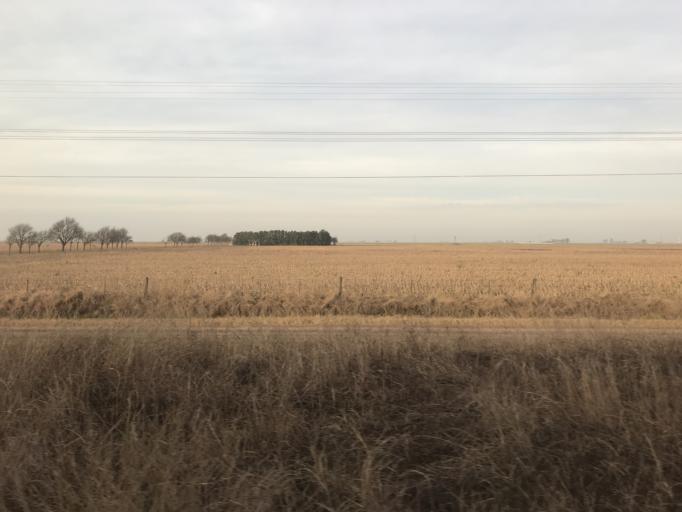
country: AR
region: Cordoba
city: Marcos Juarez
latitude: -32.6859
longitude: -62.1792
